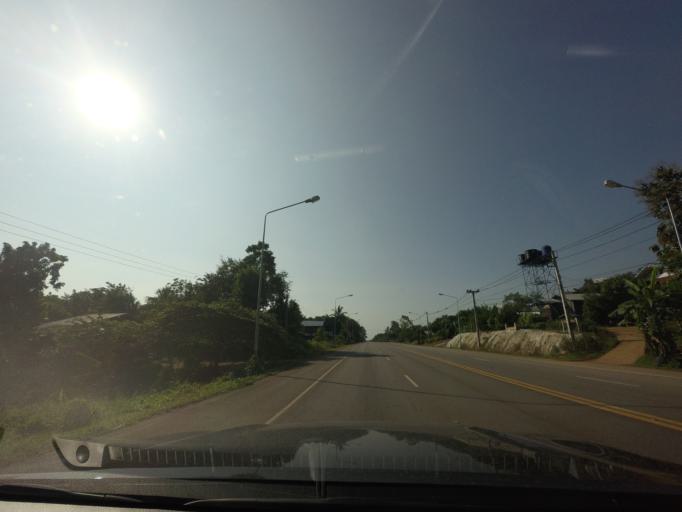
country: TH
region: Phetchabun
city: Lom Kao
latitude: 16.8641
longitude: 101.1713
